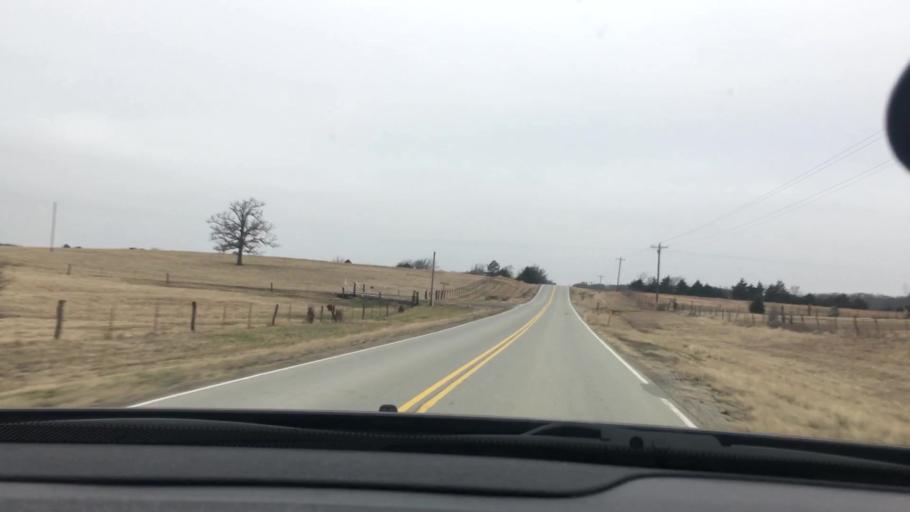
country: US
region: Oklahoma
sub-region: Coal County
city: Coalgate
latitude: 34.5056
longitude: -96.3205
